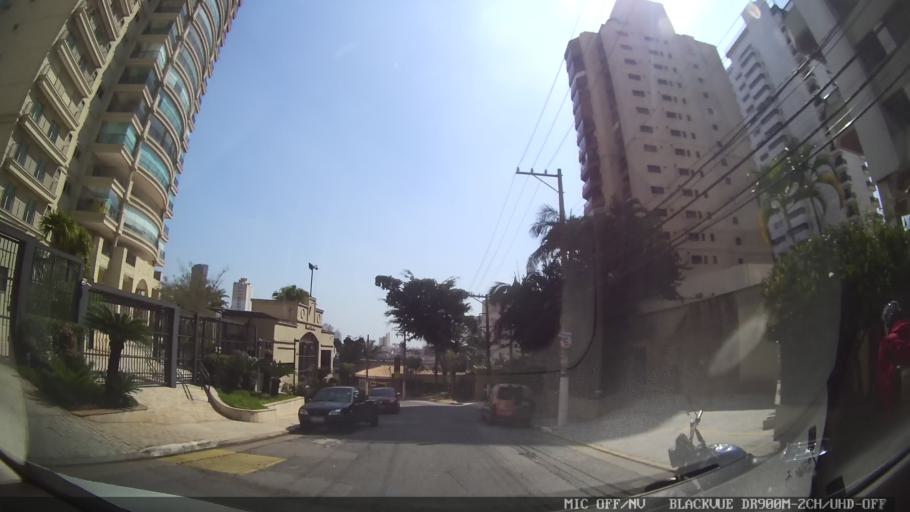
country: BR
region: Sao Paulo
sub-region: Sao Paulo
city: Sao Paulo
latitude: -23.4880
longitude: -46.6309
